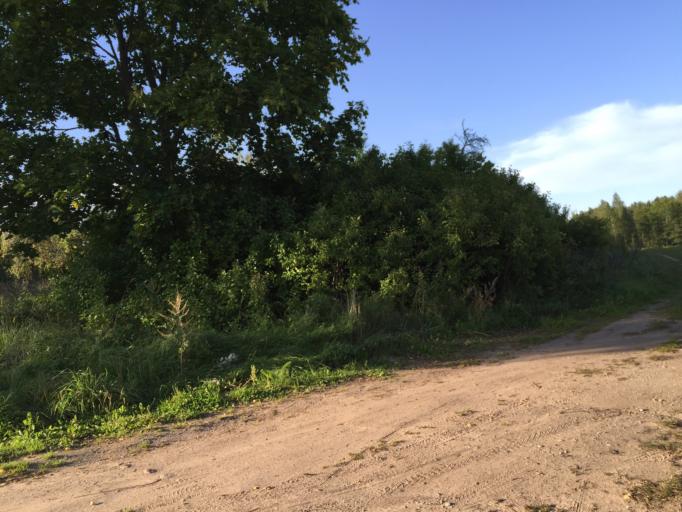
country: LT
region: Panevezys
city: Rokiskis
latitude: 55.8838
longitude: 25.6919
